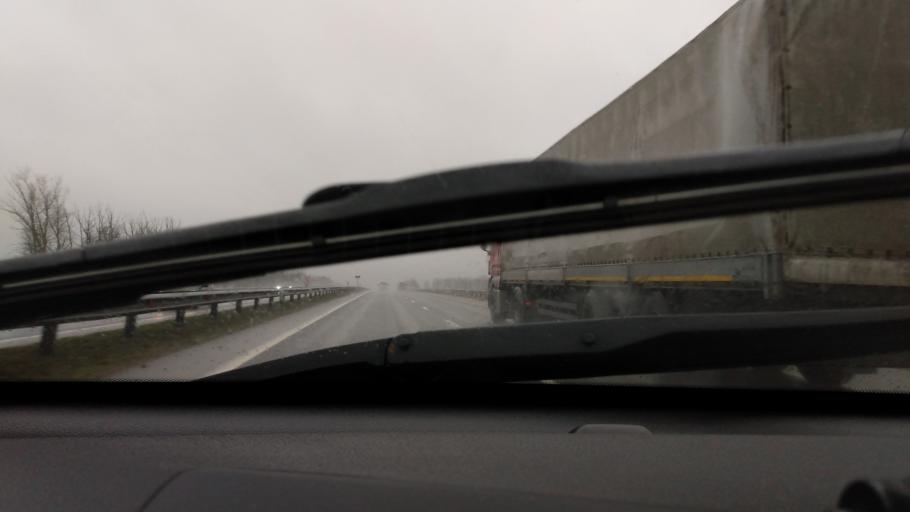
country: RU
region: Tula
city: Gritsovskiy
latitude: 54.2232
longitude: 38.1172
